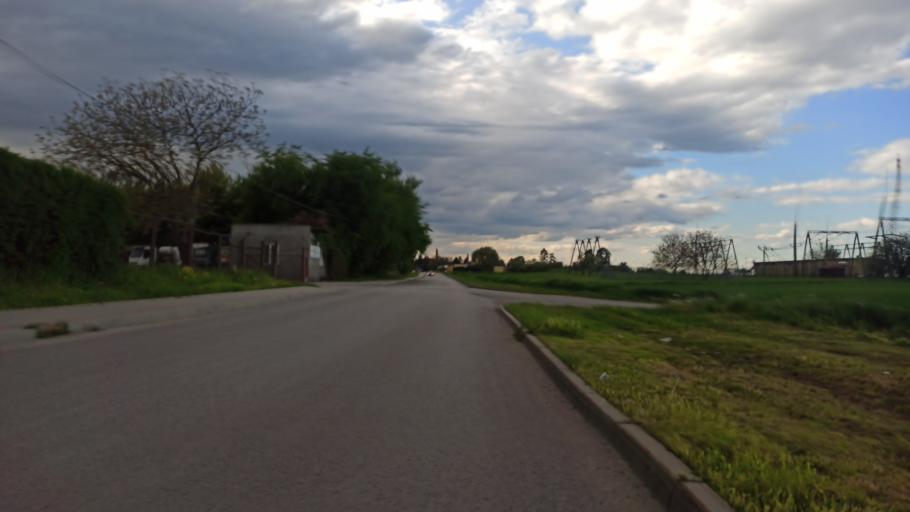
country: PL
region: Subcarpathian Voivodeship
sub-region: Powiat jaroslawski
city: Radymno
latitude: 49.9347
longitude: 22.8381
